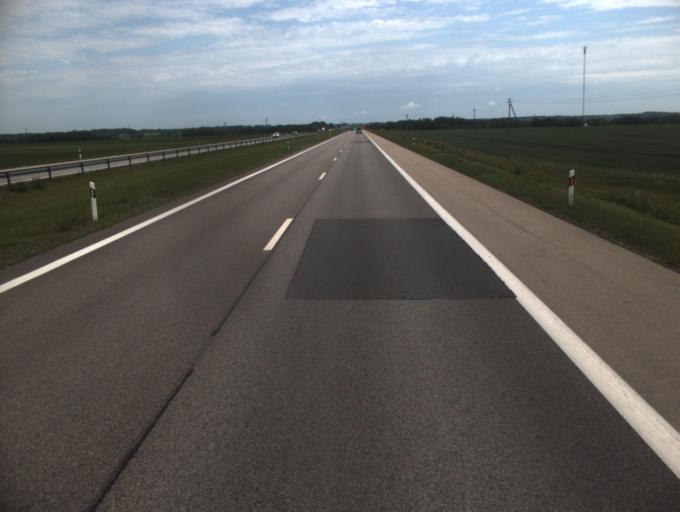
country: LT
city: Raseiniai
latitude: 55.3311
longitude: 23.1269
